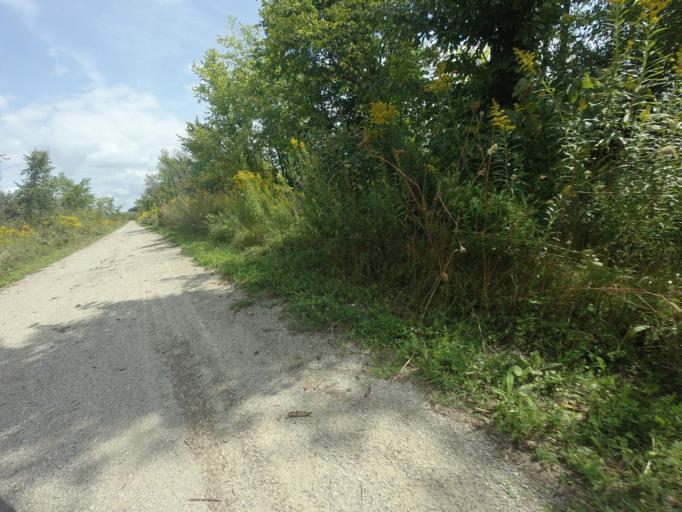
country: CA
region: Ontario
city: North Perth
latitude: 43.5733
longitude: -80.8458
